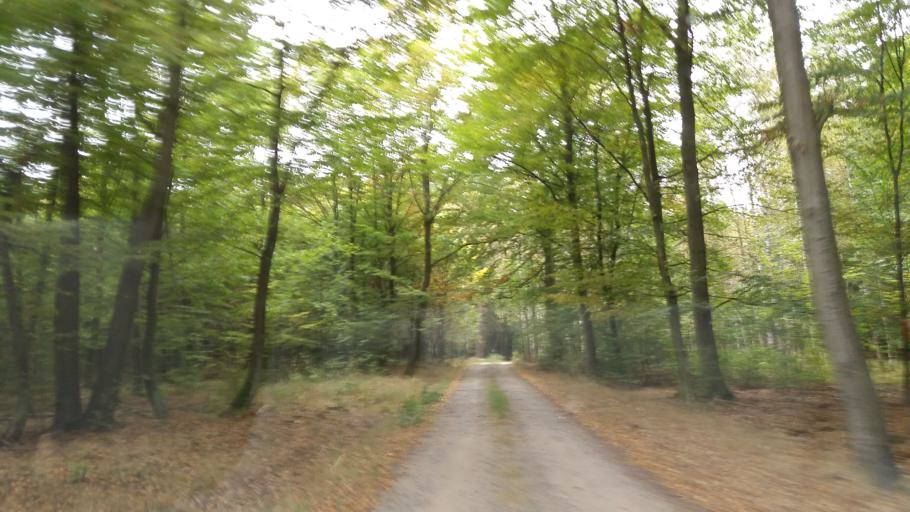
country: PL
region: West Pomeranian Voivodeship
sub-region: Powiat choszczenski
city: Pelczyce
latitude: 52.9624
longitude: 15.3209
